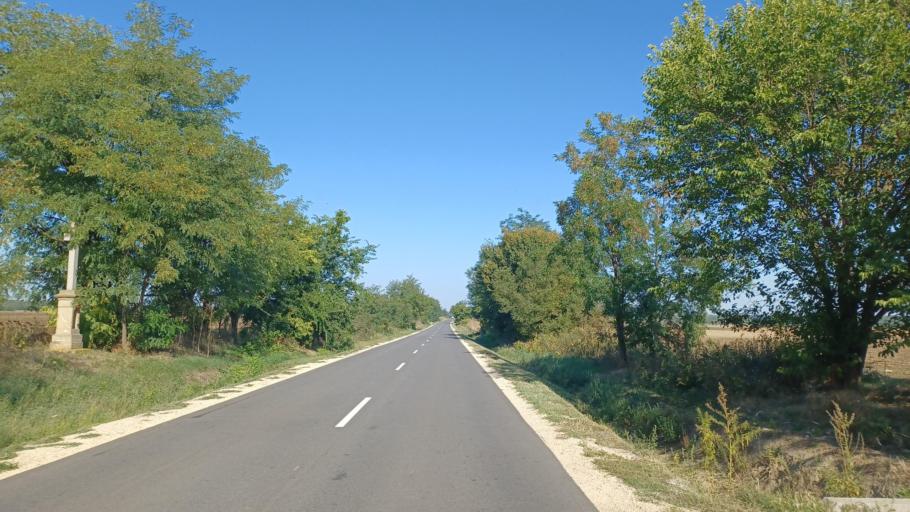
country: HU
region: Tolna
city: Paks
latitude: 46.6632
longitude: 18.8260
